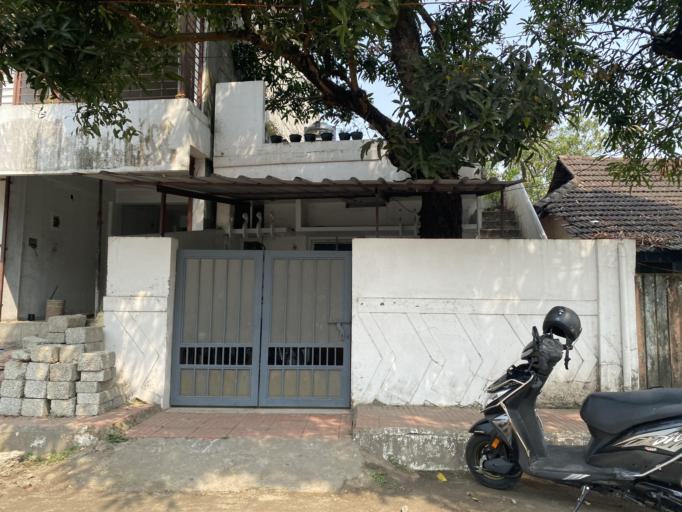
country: IN
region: Kerala
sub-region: Ernakulam
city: Cochin
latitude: 9.9503
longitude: 76.2533
